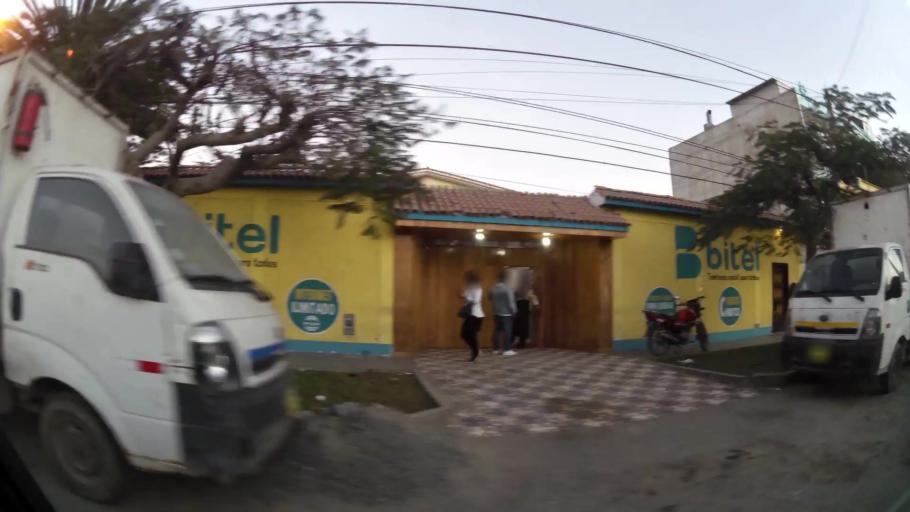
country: PE
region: Ancash
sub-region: Provincia de Santa
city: Buenos Aires
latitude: -9.1224
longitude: -78.5336
